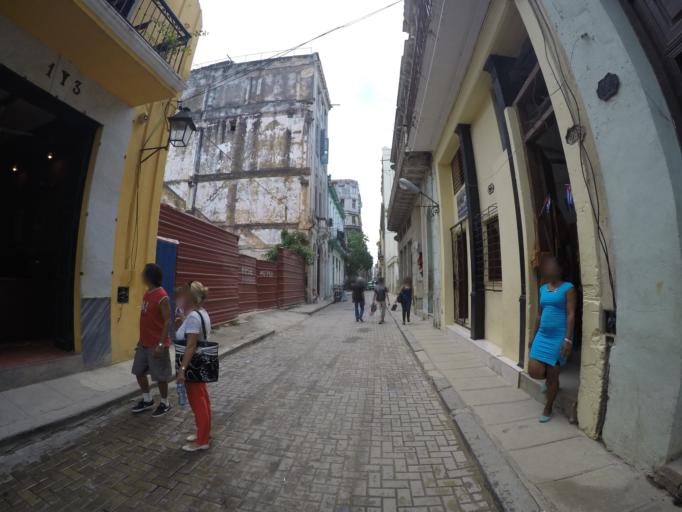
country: CU
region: La Habana
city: La Habana Vieja
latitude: 23.1398
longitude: -82.3517
